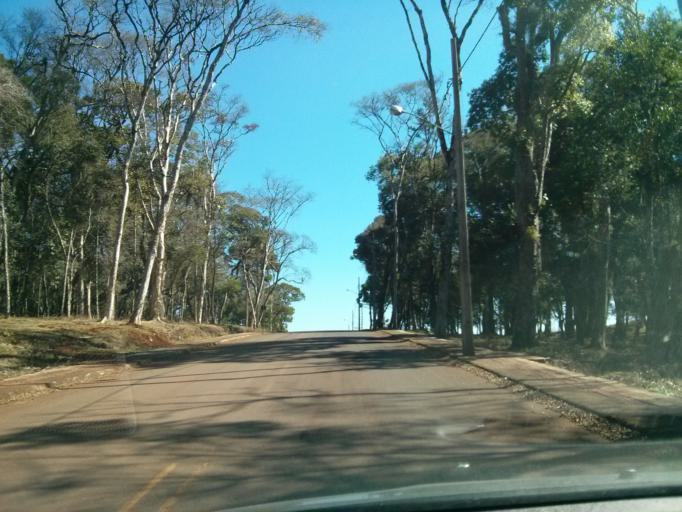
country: BR
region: Santa Catarina
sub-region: Chapeco
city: Chapeco
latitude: -27.0888
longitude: -52.6909
